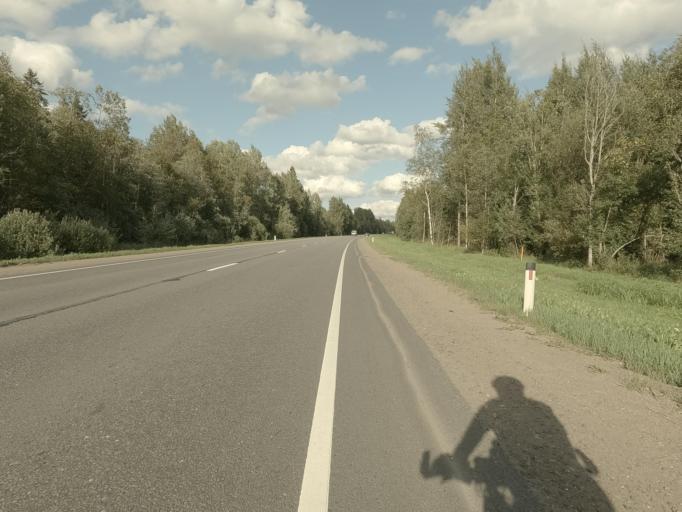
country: RU
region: Leningrad
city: Nikol'skoye
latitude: 59.6666
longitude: 30.8851
